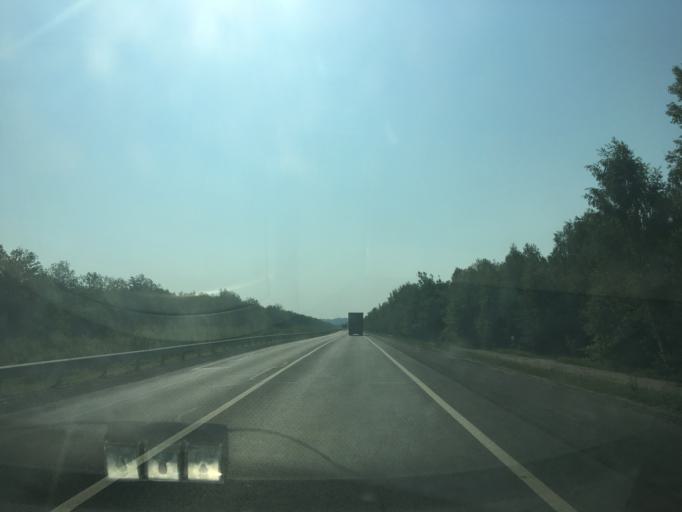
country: RU
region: Nizjnij Novgorod
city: Kstovo
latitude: 56.0906
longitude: 44.3315
